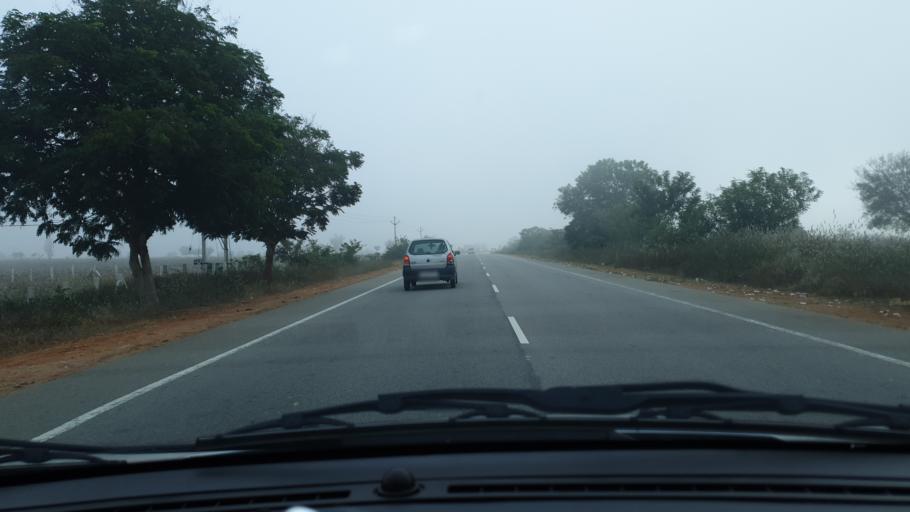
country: IN
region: Telangana
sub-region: Nalgonda
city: Devarkonda
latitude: 16.6317
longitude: 78.6540
